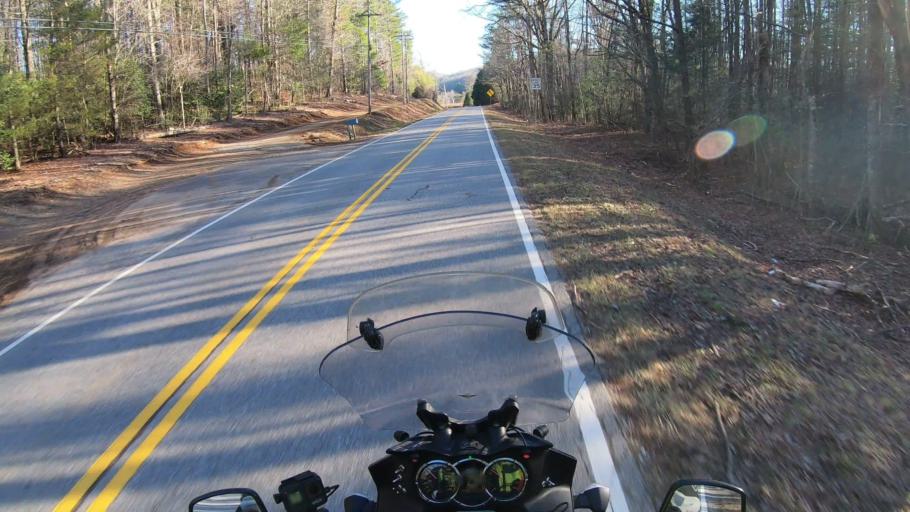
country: US
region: Georgia
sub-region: Lumpkin County
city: Dahlonega
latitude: 34.7087
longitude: -84.0427
